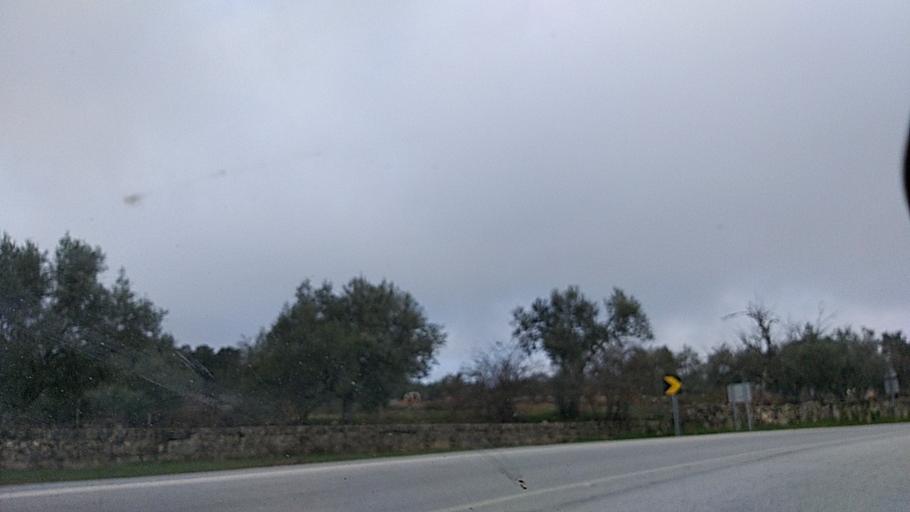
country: PT
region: Guarda
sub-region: Fornos de Algodres
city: Fornos de Algodres
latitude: 40.7200
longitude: -7.4910
